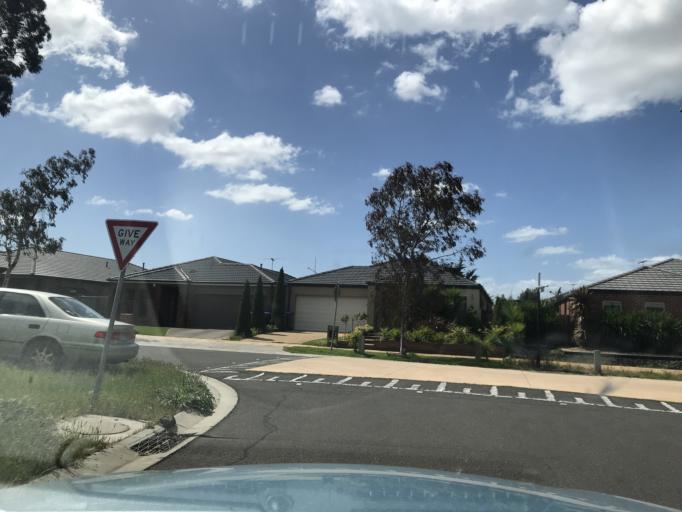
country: AU
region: Victoria
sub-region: Wyndham
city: Williams Landing
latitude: -37.8590
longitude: 144.7344
